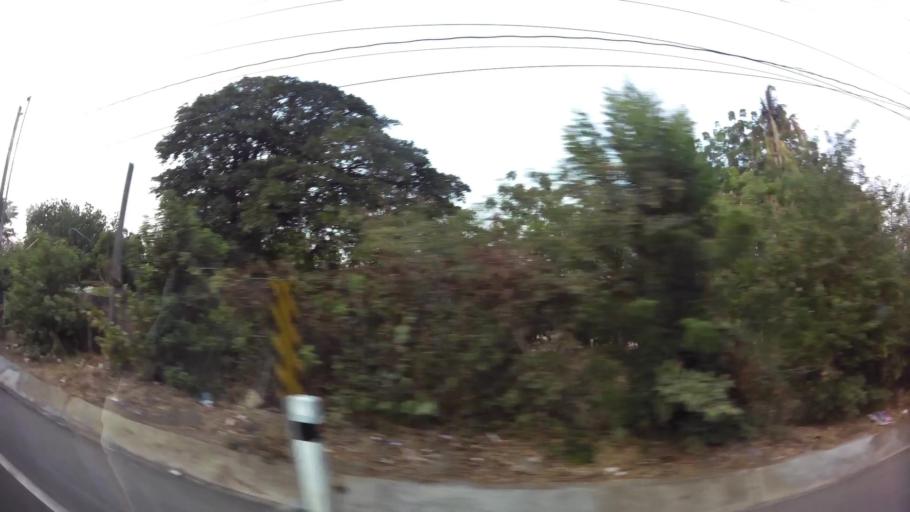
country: NI
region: Managua
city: Ciudad Sandino
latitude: 12.1789
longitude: -86.3535
